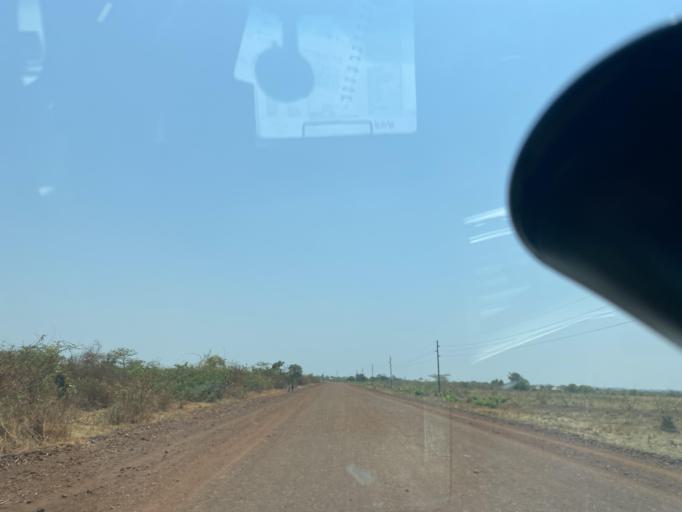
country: ZM
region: Southern
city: Nakambala
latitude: -15.4870
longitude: 27.9005
